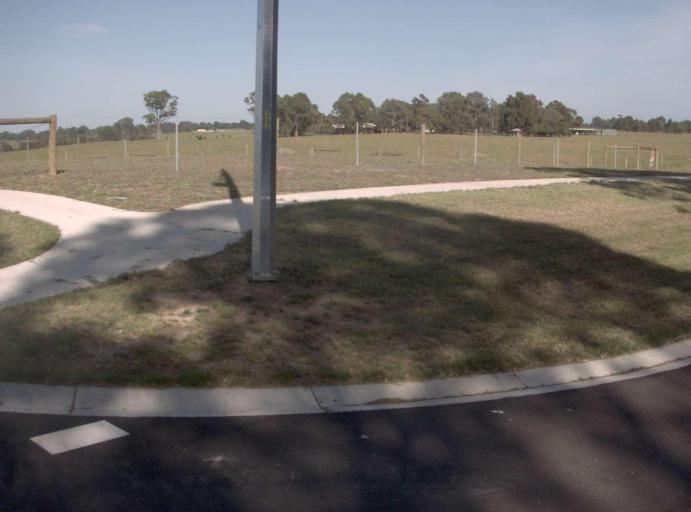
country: AU
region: Victoria
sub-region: East Gippsland
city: Lakes Entrance
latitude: -37.8205
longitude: 147.8547
